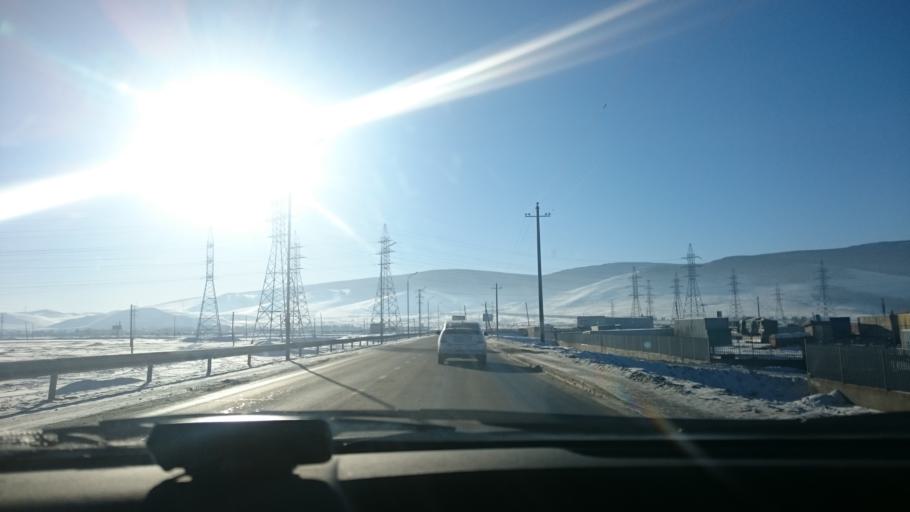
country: MN
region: Ulaanbaatar
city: Ulaanbaatar
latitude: 47.9042
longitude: 107.0350
